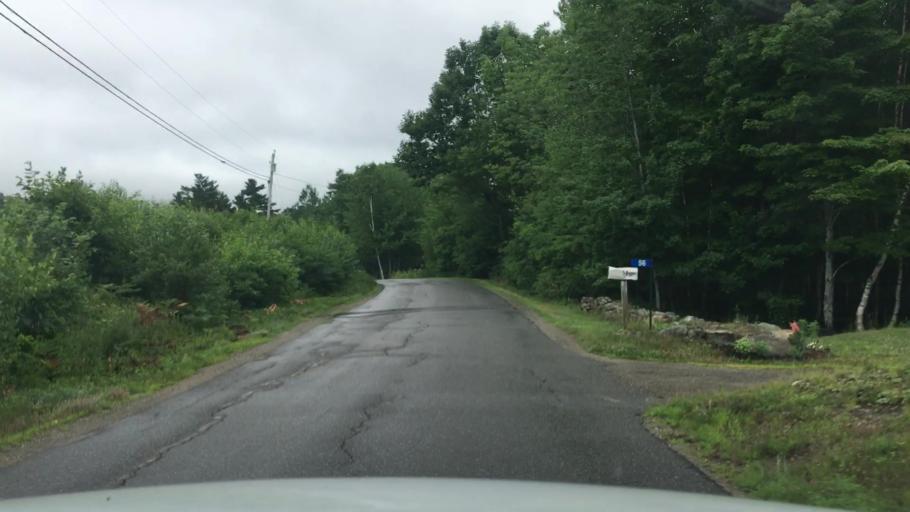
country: US
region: Maine
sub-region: Knox County
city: Hope
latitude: 44.2254
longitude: -69.1779
